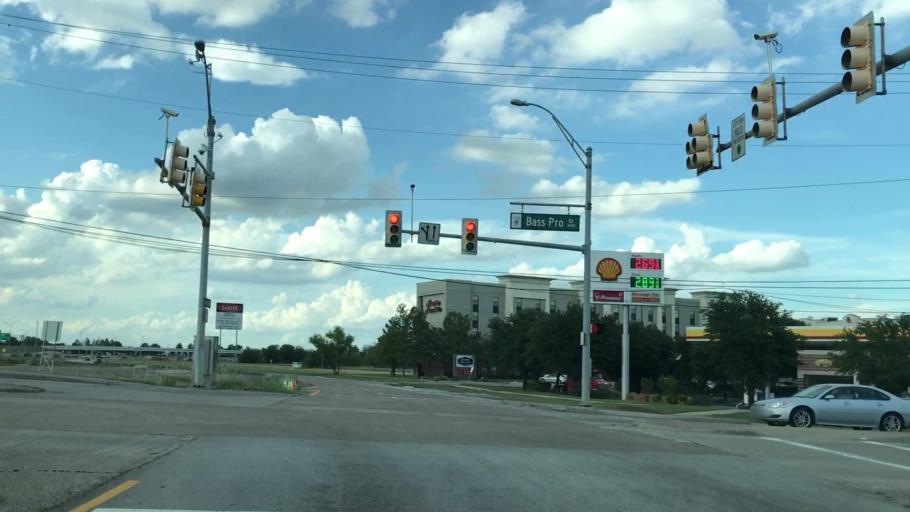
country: US
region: Texas
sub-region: Dallas County
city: Coppell
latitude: 32.9550
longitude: -97.0380
